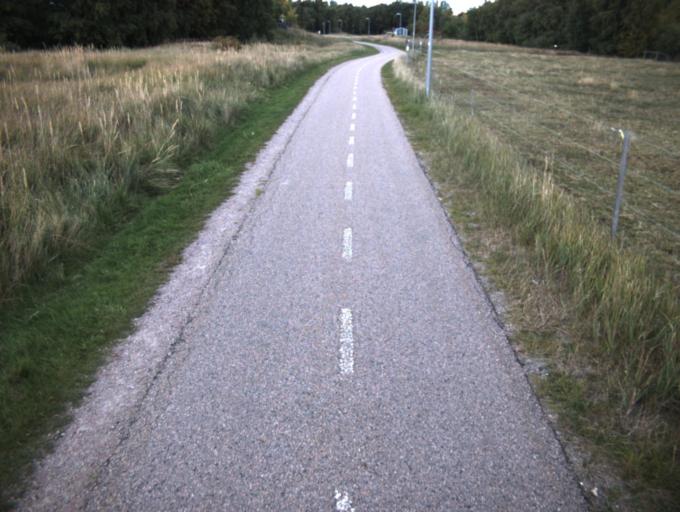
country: SE
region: Skane
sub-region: Helsingborg
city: Rydeback
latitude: 55.9857
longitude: 12.7533
